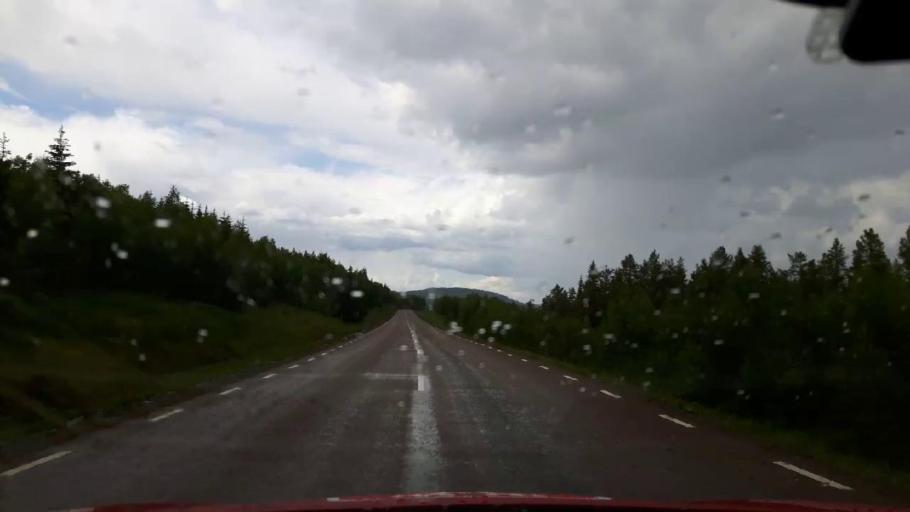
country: SE
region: Jaemtland
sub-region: Krokoms Kommun
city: Valla
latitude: 63.8898
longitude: 14.2724
